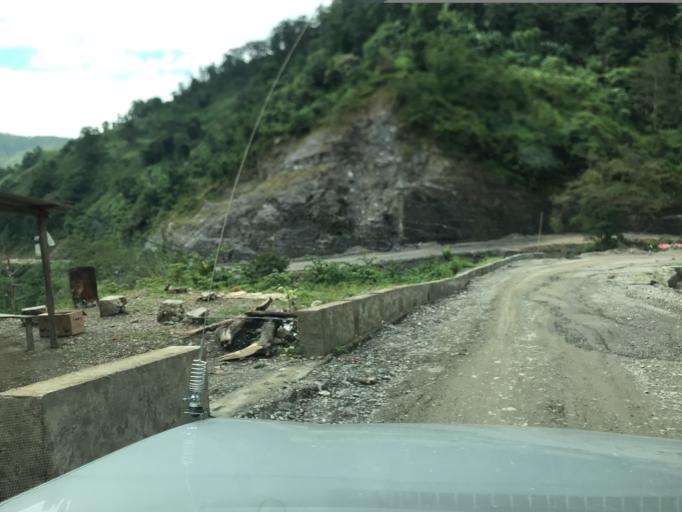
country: TL
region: Aileu
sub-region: Aileu Villa
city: Aileu
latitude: -8.6470
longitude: 125.5248
